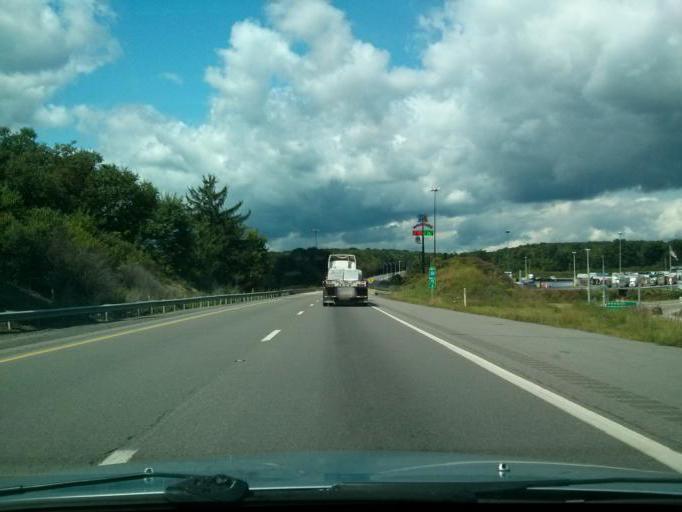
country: US
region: Pennsylvania
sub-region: Jefferson County
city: Brookville
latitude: 41.1707
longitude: -79.0962
